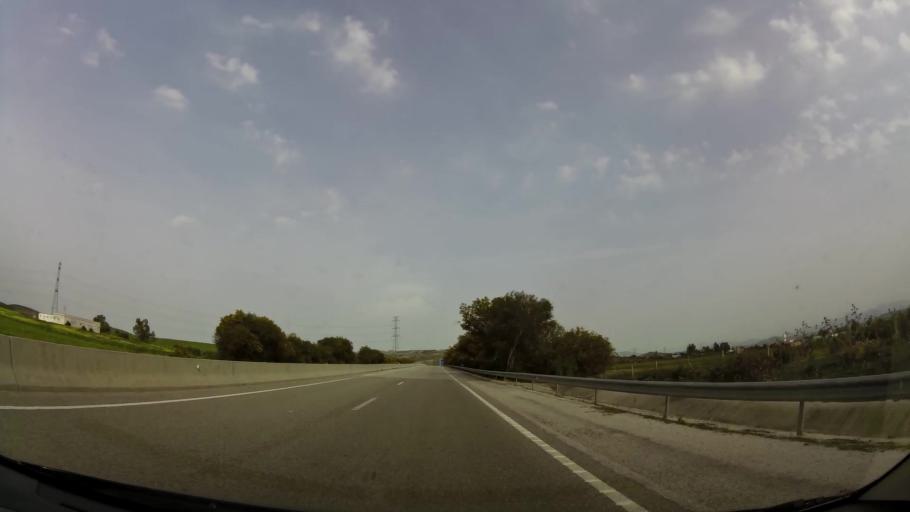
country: MA
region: Tanger-Tetouan
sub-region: Tanger-Assilah
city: Tangier
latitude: 35.6687
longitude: -5.7660
